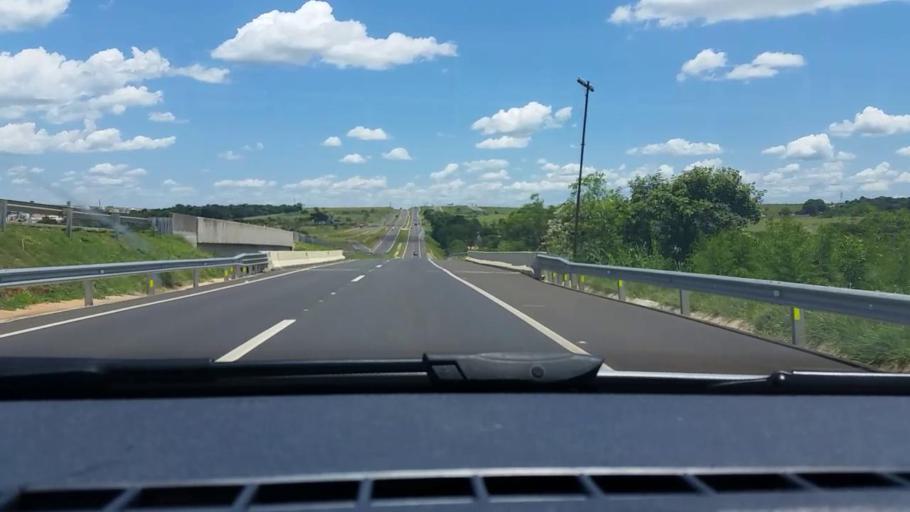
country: BR
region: Sao Paulo
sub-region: Bauru
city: Bauru
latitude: -22.3822
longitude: -49.0670
